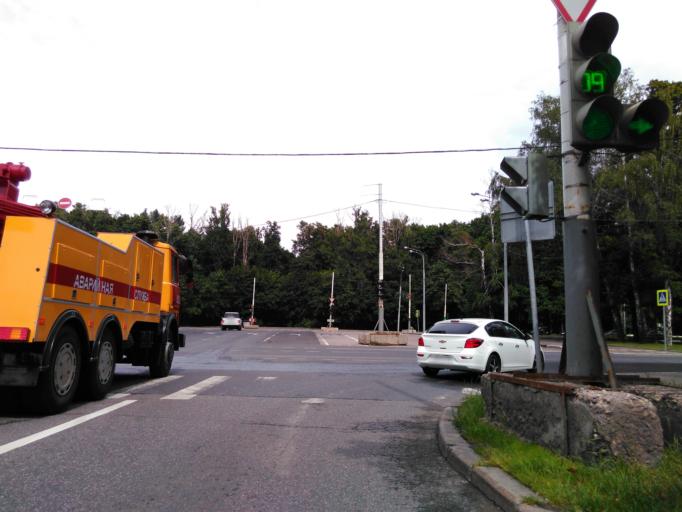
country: RU
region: Moscow
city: Vorob'yovo
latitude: 55.7076
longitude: 37.5329
